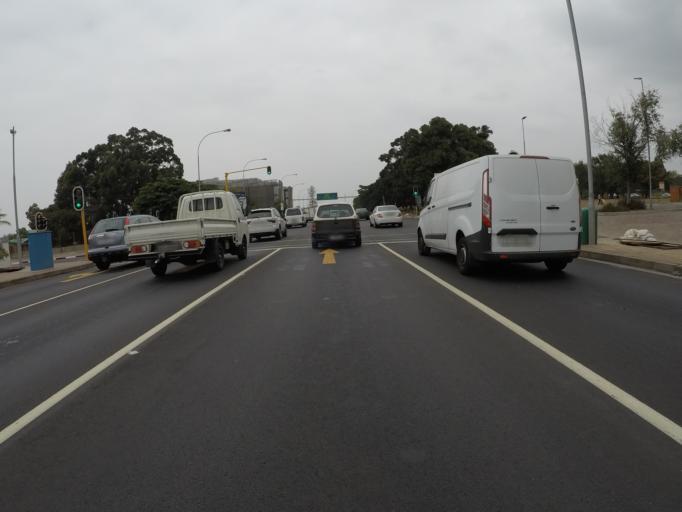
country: ZA
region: Western Cape
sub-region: City of Cape Town
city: Kraaifontein
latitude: -33.8841
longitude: 18.6357
